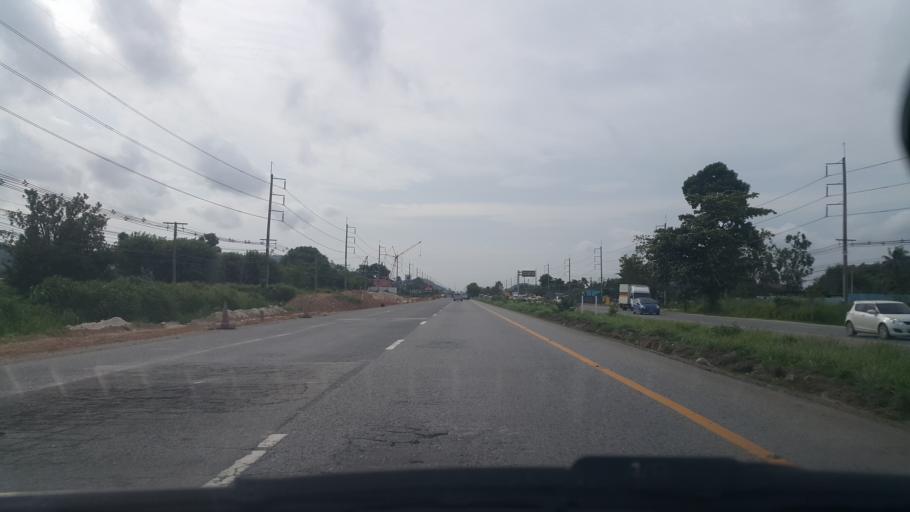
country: TH
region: Rayong
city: Nikhom Phattana
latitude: 12.7990
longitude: 101.1492
